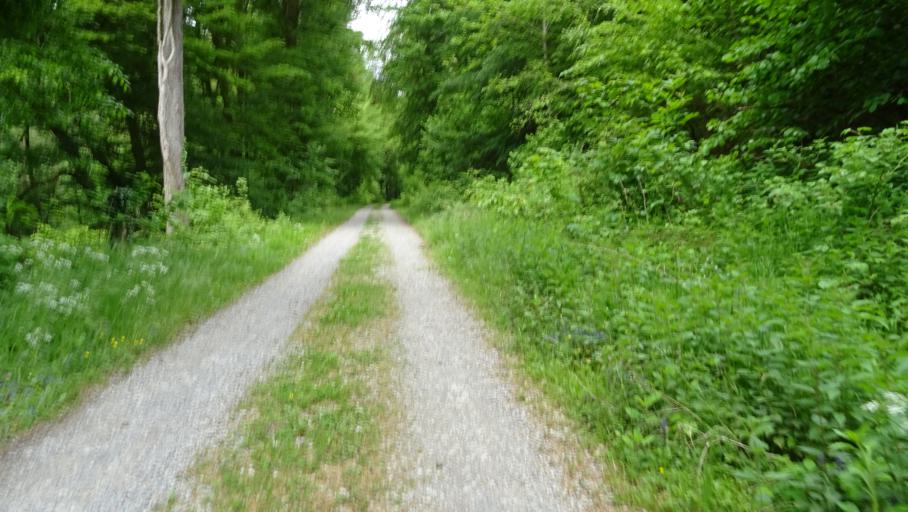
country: DE
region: Baden-Wuerttemberg
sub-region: Karlsruhe Region
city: Neckargerach
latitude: 49.4178
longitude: 9.0962
